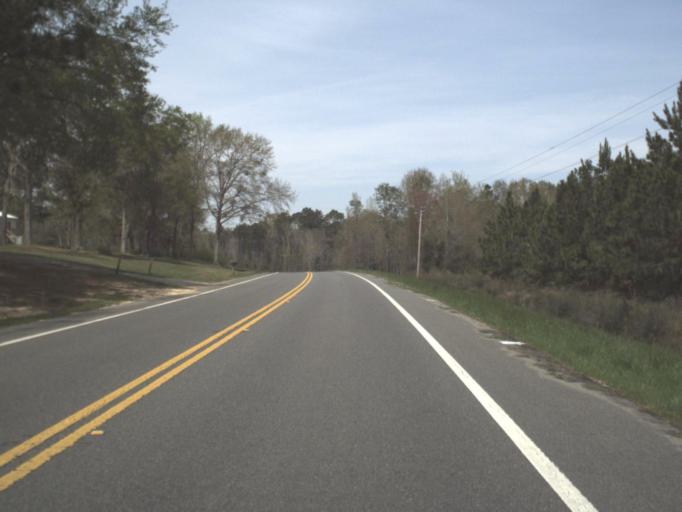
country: US
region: Alabama
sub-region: Geneva County
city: Geneva
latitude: 30.9344
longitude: -85.9672
